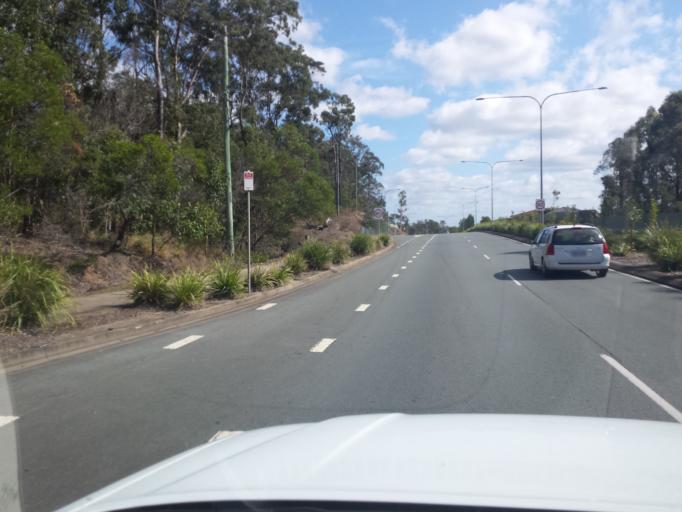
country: AU
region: Queensland
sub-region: Brisbane
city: Bridegman Downs
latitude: -27.3744
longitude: 152.9803
